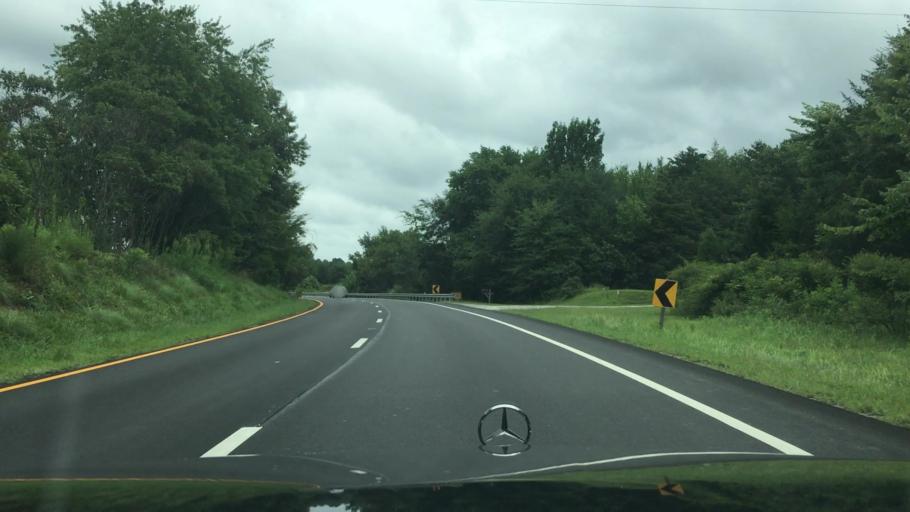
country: US
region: Virginia
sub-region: Prince Edward County
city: Farmville
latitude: 37.2737
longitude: -78.3100
